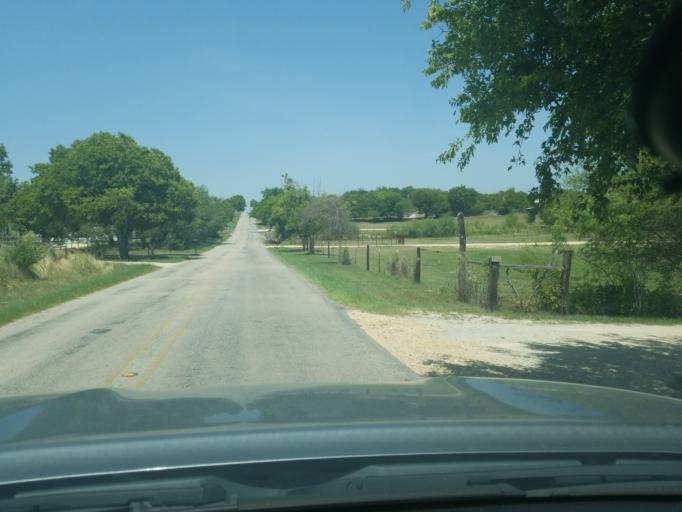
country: US
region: Texas
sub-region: Guadalupe County
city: Cibolo
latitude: 29.5837
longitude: -98.2081
